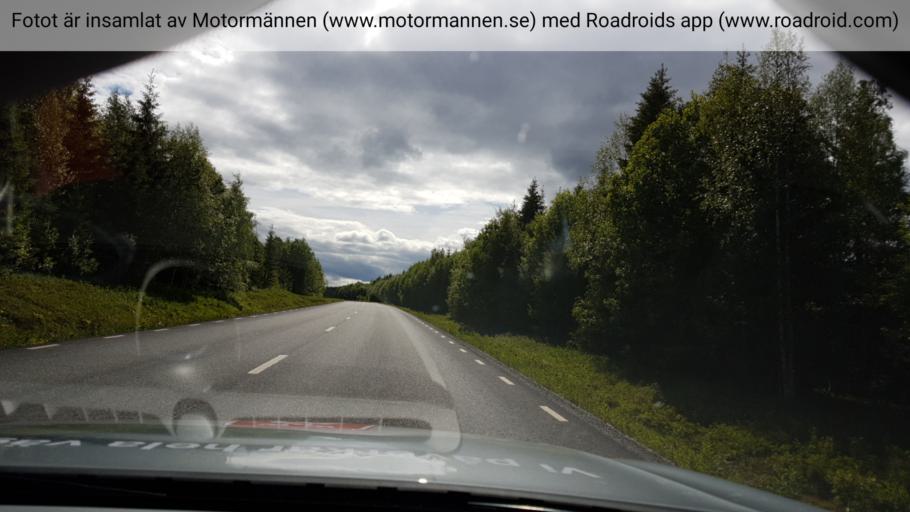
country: SE
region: Jaemtland
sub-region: Stroemsunds Kommun
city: Stroemsund
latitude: 64.1249
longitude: 15.6372
